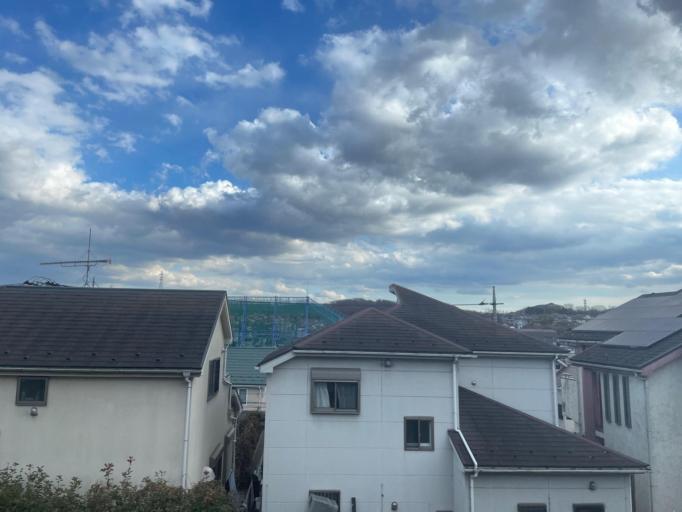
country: JP
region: Tokyo
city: Hachioji
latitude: 35.6443
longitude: 139.3428
